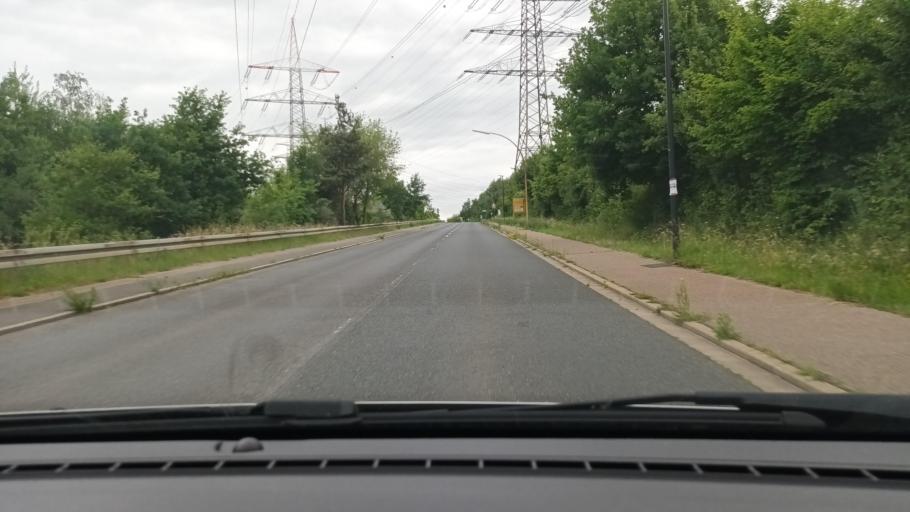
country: DE
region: North Rhine-Westphalia
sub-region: Regierungsbezirk Koln
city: Hurth
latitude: 50.8637
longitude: 6.8494
